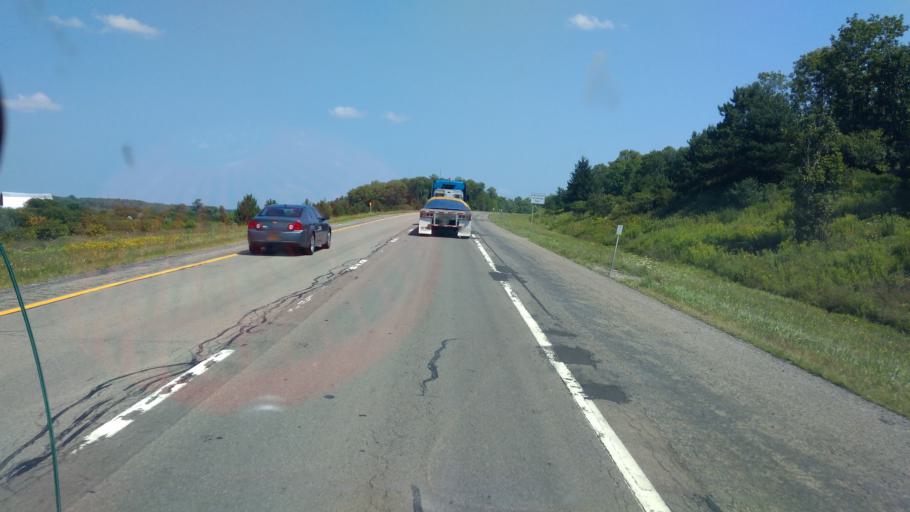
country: US
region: New York
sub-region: Allegany County
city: Alfred
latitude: 42.3095
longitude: -77.8651
